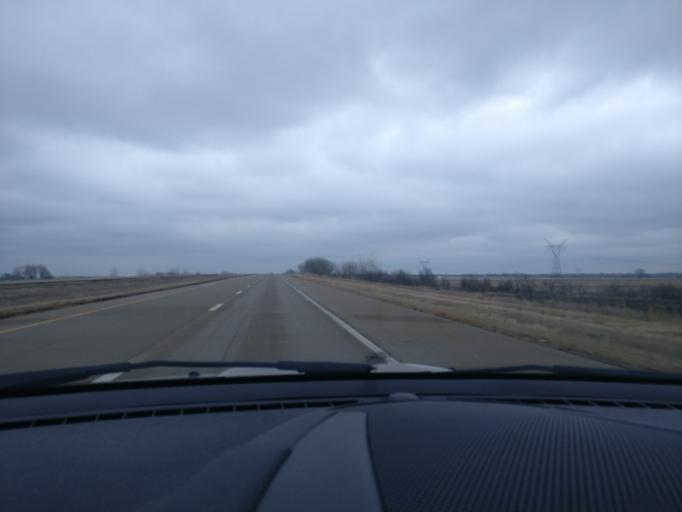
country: US
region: Illinois
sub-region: Whiteside County
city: Morrison
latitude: 41.7654
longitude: -89.8377
